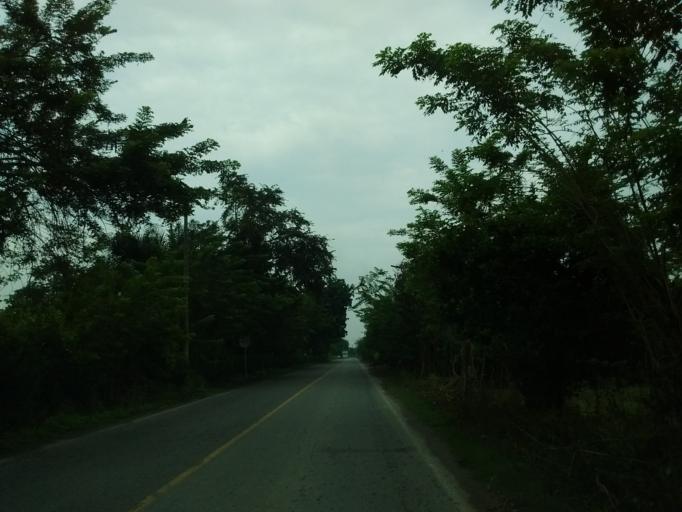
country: CO
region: Cauca
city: Padilla
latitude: 3.2303
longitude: -76.3290
